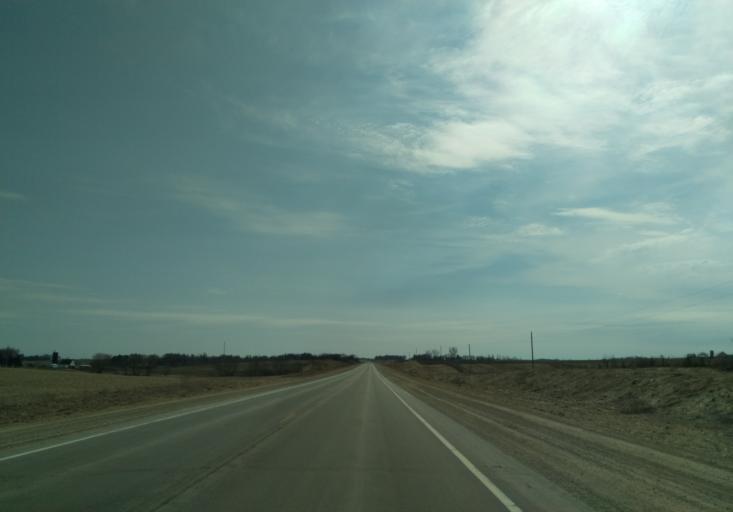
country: US
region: Minnesota
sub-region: Fillmore County
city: Harmony
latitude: 43.4712
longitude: -91.8700
